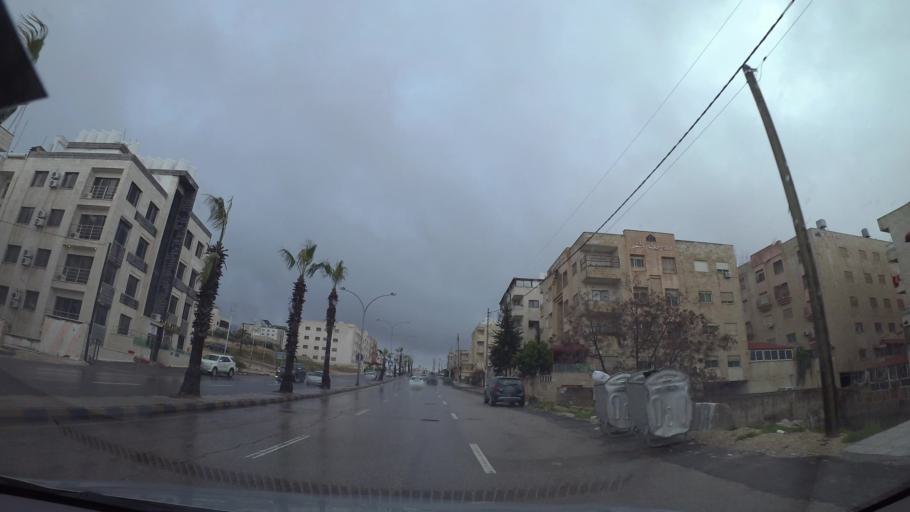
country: JO
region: Amman
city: Al Jubayhah
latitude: 32.0320
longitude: 35.8630
